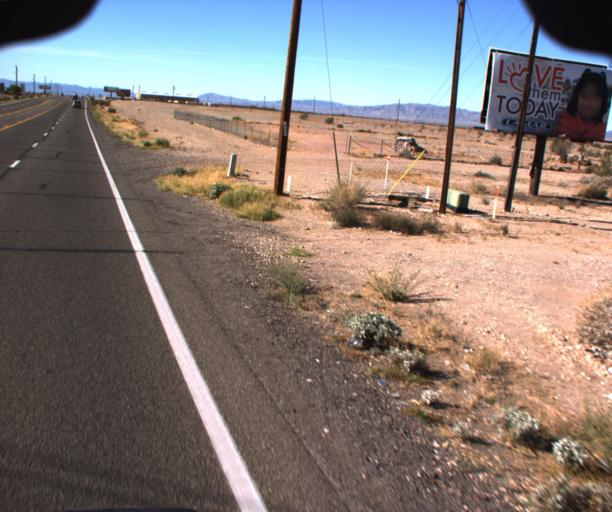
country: US
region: Arizona
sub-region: Mohave County
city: Mohave Valley
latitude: 34.9899
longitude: -114.5981
